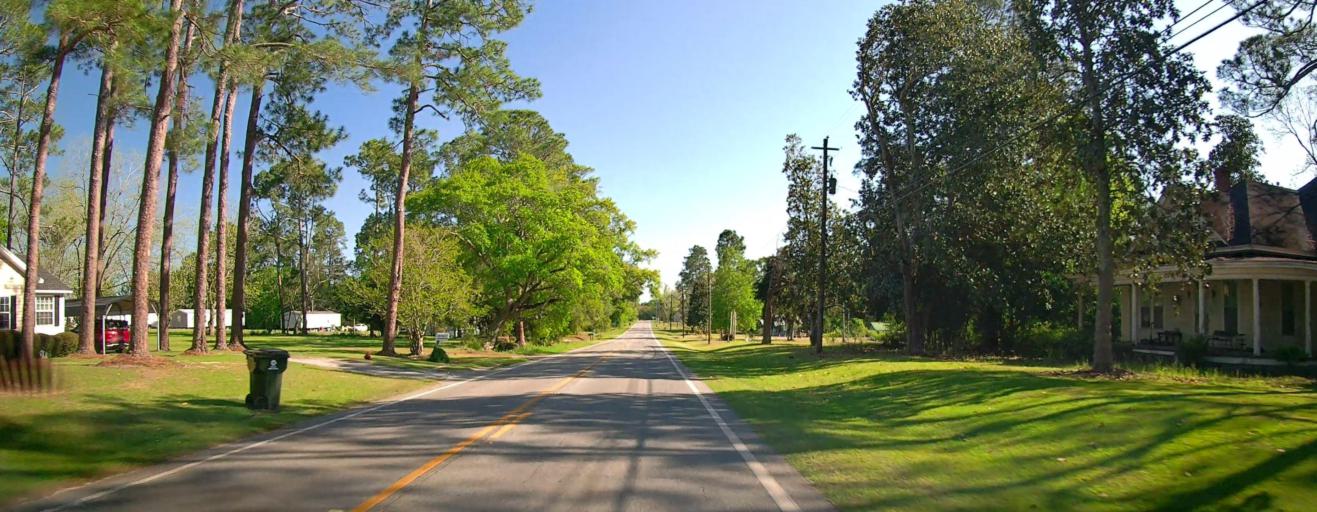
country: US
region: Georgia
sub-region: Wilcox County
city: Rochelle
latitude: 31.9423
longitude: -83.4564
